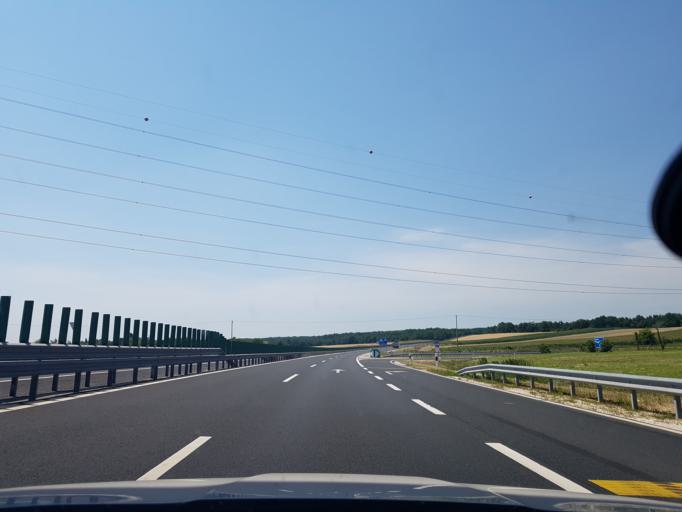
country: HU
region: Vas
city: Sarvar
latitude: 47.3024
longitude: 16.8376
